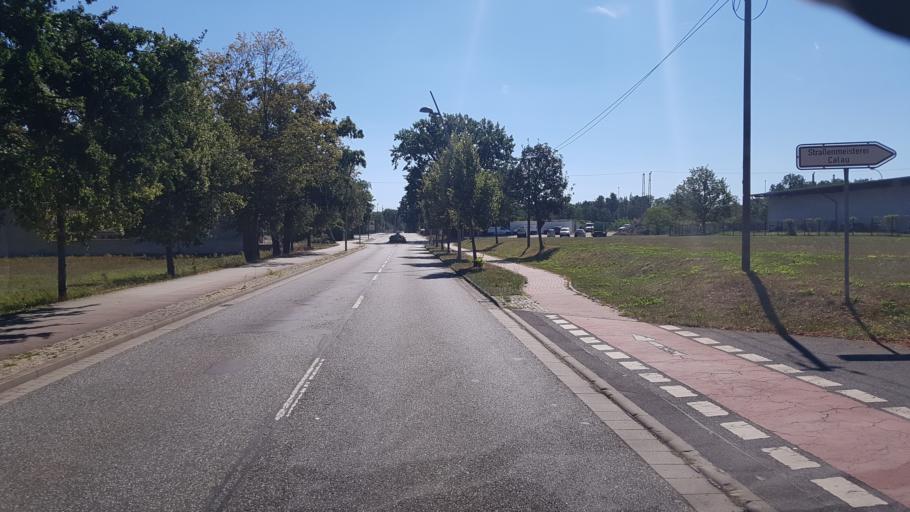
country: DE
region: Brandenburg
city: Calau
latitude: 51.7370
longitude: 13.9732
